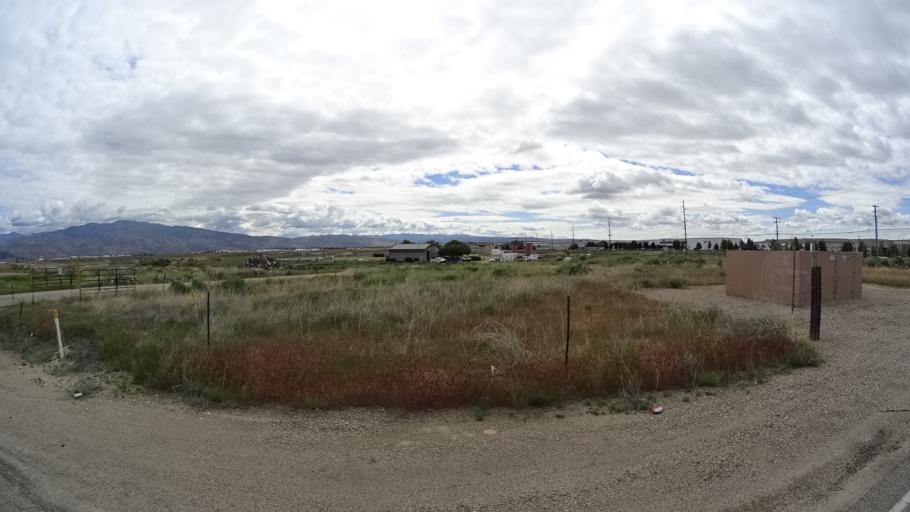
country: US
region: Idaho
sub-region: Ada County
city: Boise
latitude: 43.5479
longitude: -116.1888
